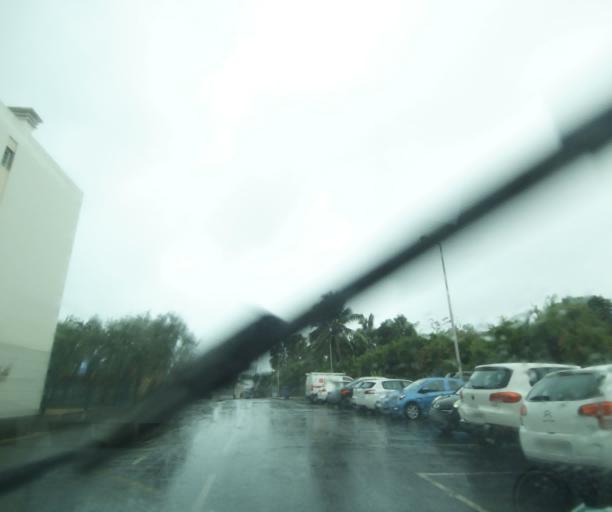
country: RE
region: Reunion
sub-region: Reunion
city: Saint-Paul
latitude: -21.0133
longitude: 55.2652
